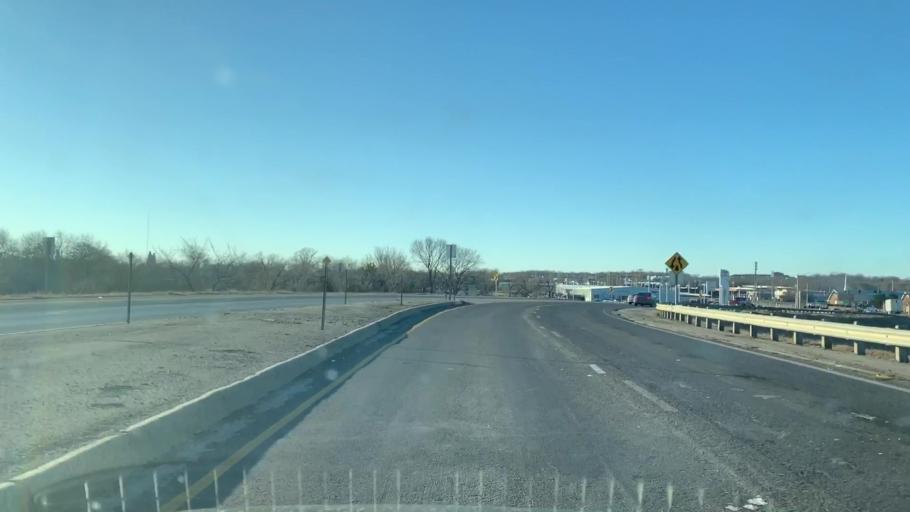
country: US
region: Kansas
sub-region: Bourbon County
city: Fort Scott
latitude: 37.8209
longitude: -94.7043
